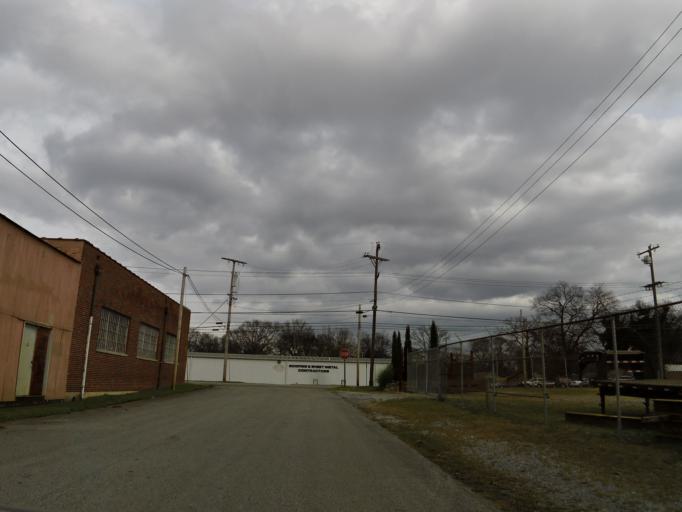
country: US
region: Tennessee
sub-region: Hamilton County
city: Chattanooga
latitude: 35.0298
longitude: -85.2917
